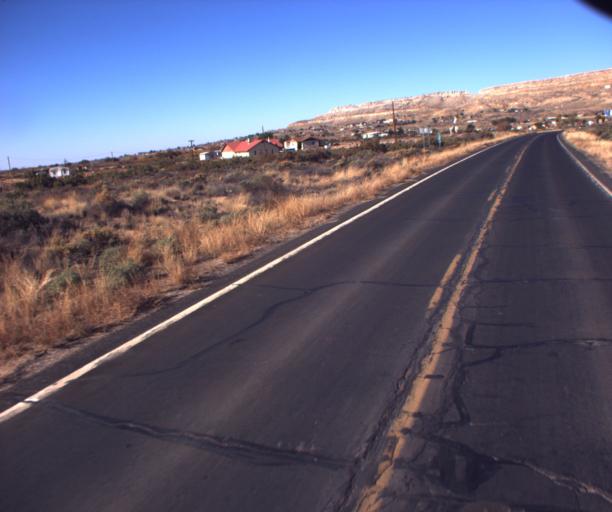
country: US
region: Arizona
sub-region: Navajo County
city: First Mesa
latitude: 35.8398
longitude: -110.3592
